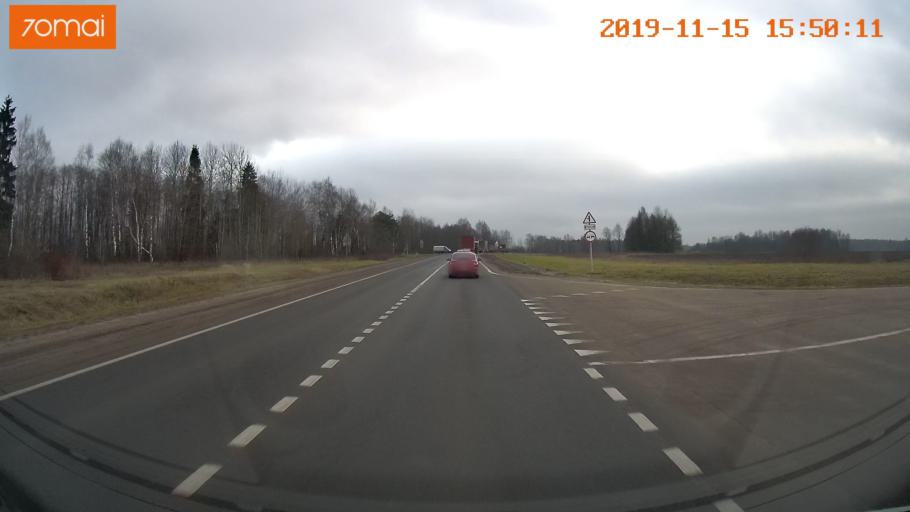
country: RU
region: Jaroslavl
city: Yaroslavl
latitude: 57.9079
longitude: 40.0126
